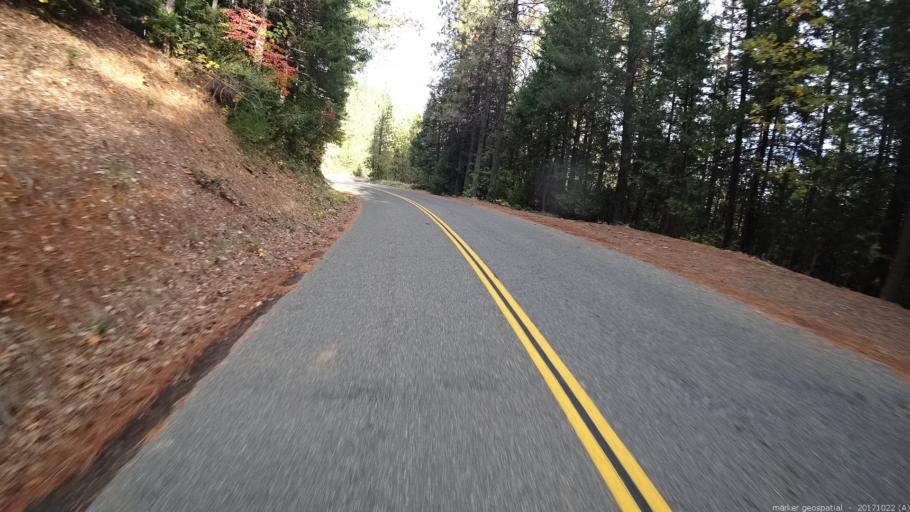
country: US
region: California
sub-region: Siskiyou County
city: Dunsmuir
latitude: 41.1541
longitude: -122.2925
